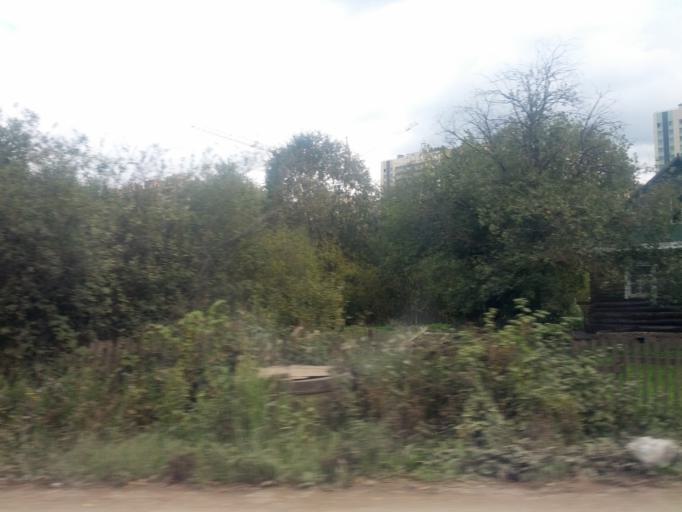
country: RU
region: Leningrad
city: Rybatskoye
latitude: 59.9062
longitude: 30.5061
